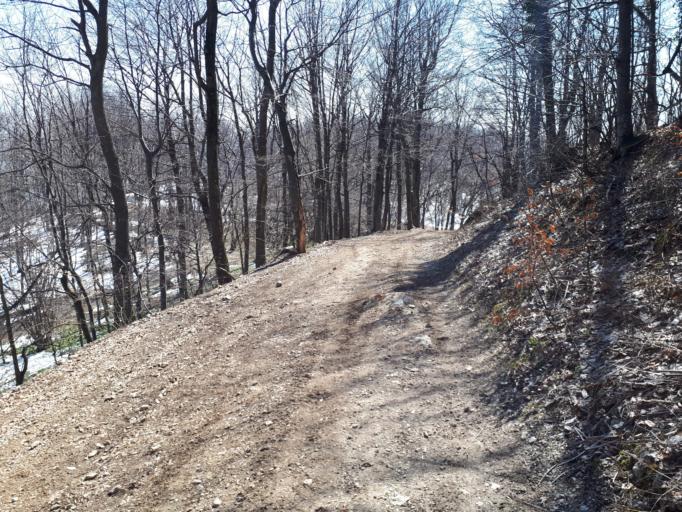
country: HR
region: Varazdinska
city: Ivanec
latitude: 46.1761
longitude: 16.1359
